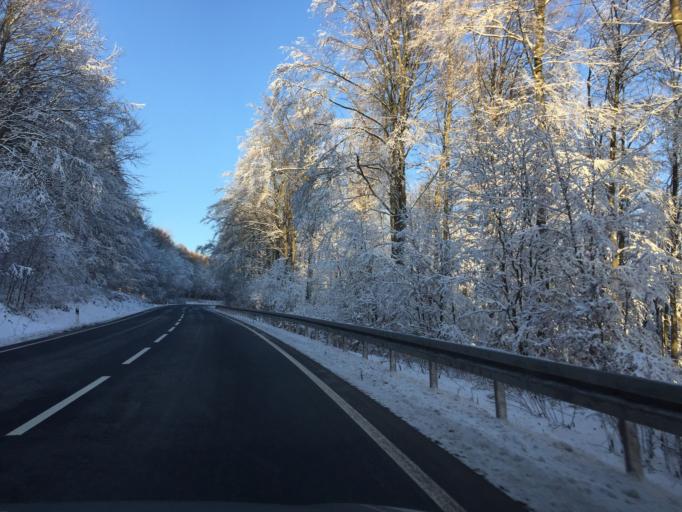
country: DE
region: Bavaria
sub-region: Regierungsbezirk Unterfranken
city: Altenbuch
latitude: 49.8941
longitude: 9.4181
